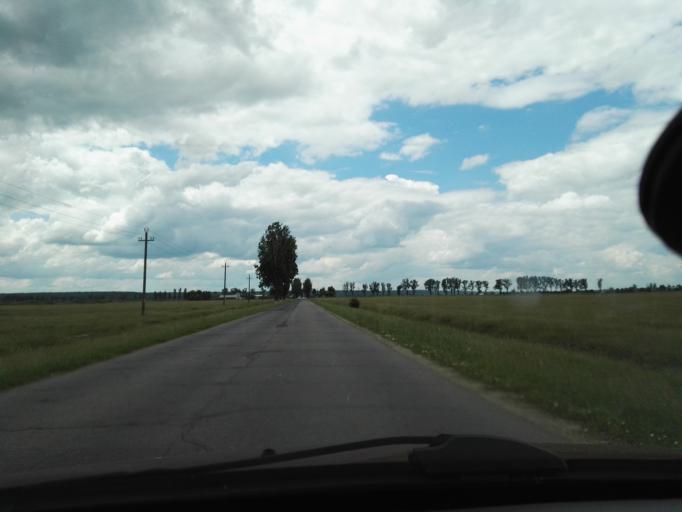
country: RO
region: Giurgiu
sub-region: Comuna Comana
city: Comana
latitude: 44.1969
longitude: 26.1397
